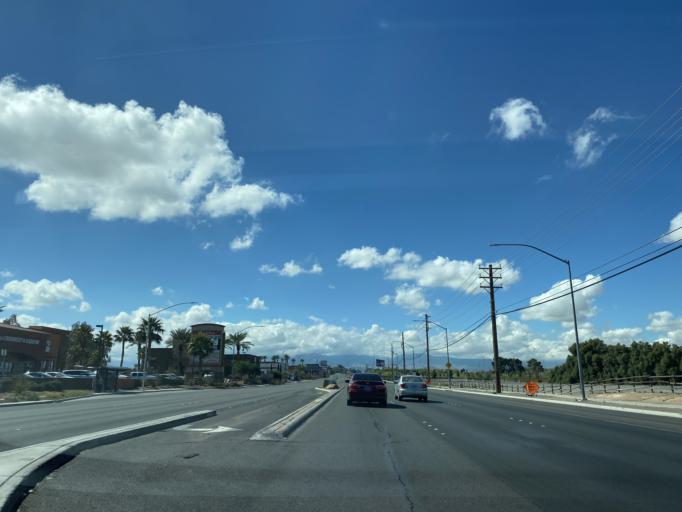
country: US
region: Nevada
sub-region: Clark County
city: North Las Vegas
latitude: 36.2395
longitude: -115.1462
